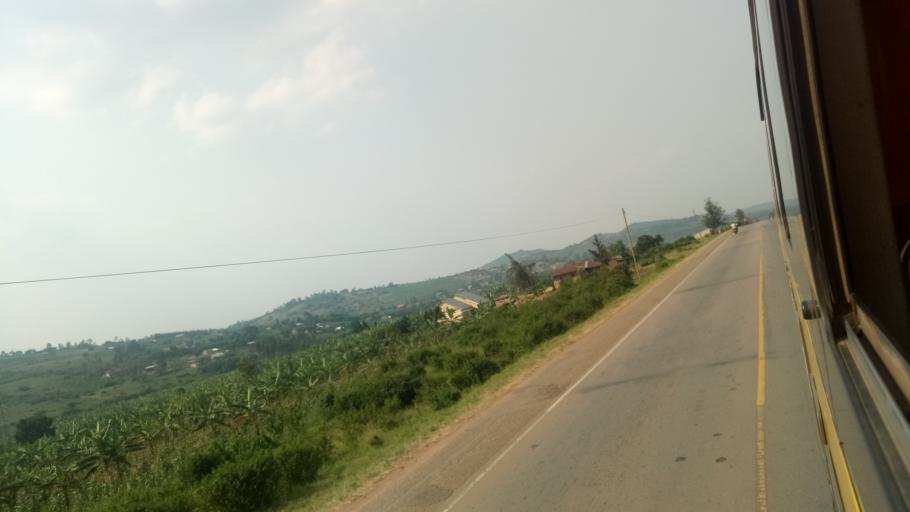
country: UG
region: Western Region
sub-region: Mbarara District
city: Mbarara
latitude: -0.5297
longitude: 30.7216
